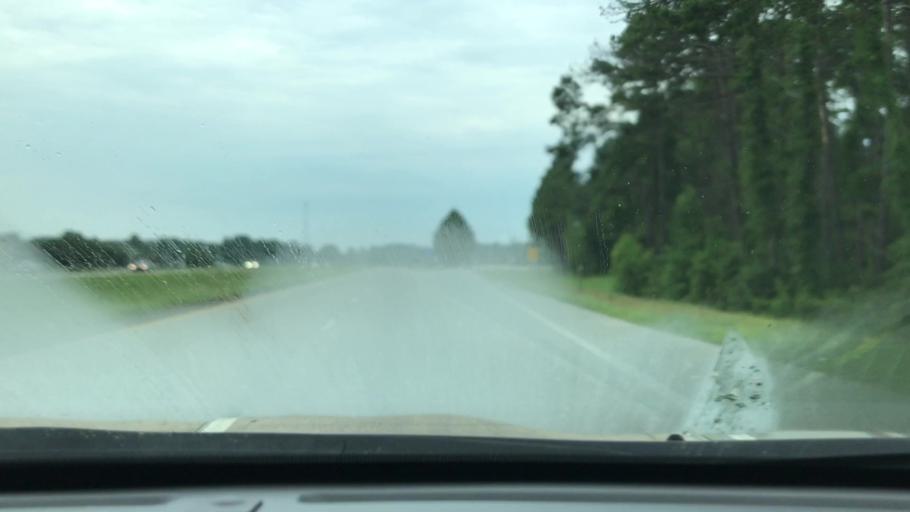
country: US
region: South Carolina
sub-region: Hampton County
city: Yemassee
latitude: 32.8049
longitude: -80.7701
